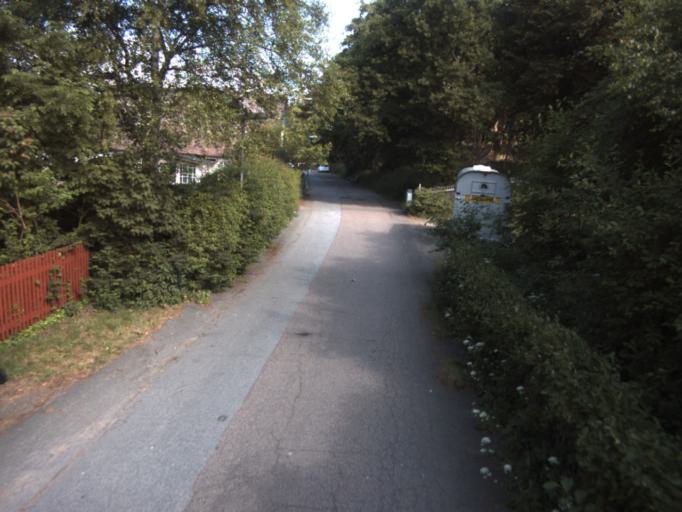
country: DK
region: Capital Region
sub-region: Helsingor Kommune
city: Helsingor
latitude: 56.1000
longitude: 12.6356
